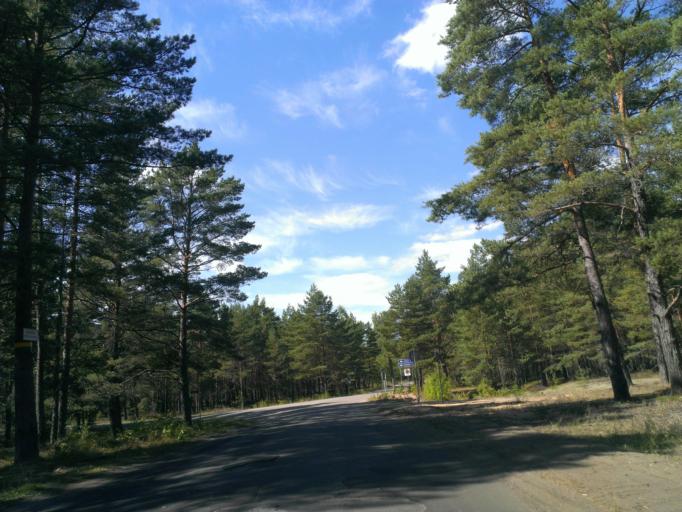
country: LV
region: Adazi
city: Adazi
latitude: 57.1043
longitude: 24.3794
